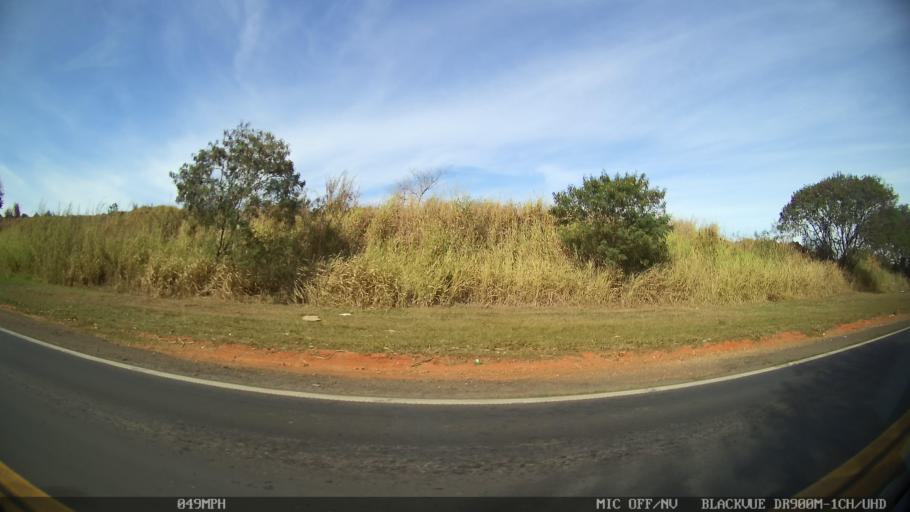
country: BR
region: Sao Paulo
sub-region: Rio Das Pedras
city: Rio das Pedras
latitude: -22.7961
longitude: -47.5982
